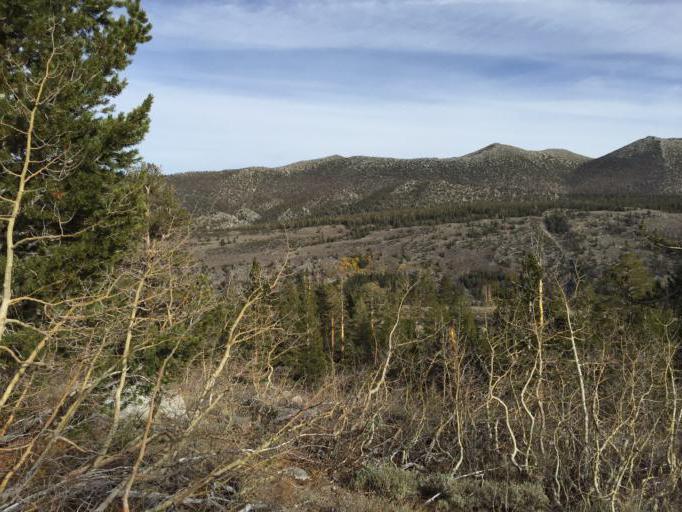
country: US
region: California
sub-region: Mono County
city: Mammoth Lakes
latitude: 37.4776
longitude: -118.7302
